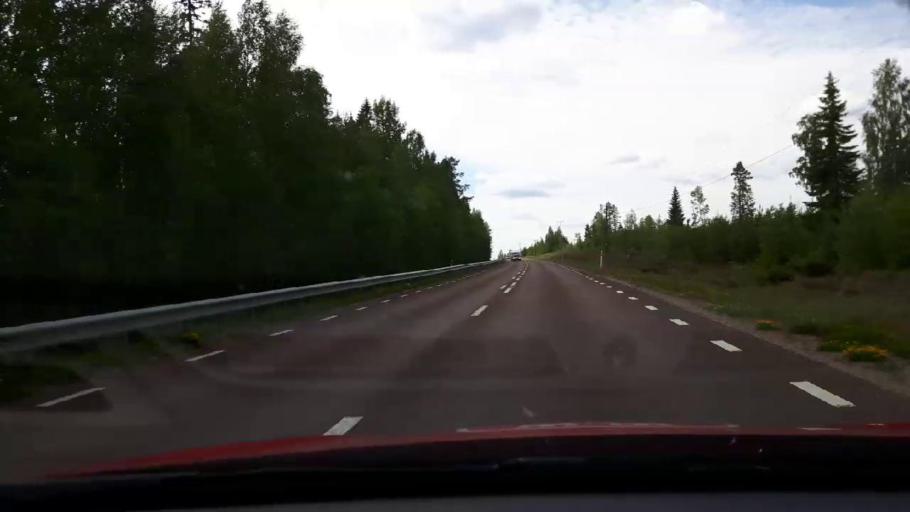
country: SE
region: Jaemtland
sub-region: Harjedalens Kommun
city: Sveg
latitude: 62.0649
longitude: 14.9225
